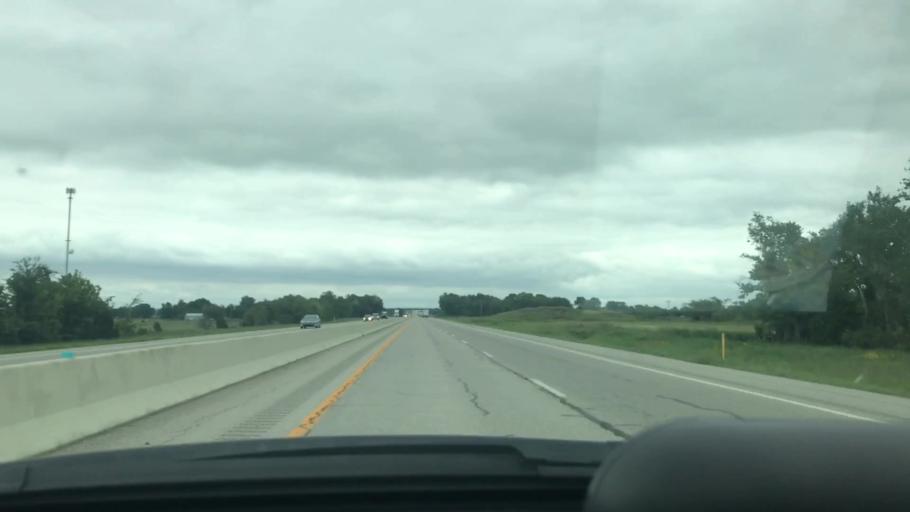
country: US
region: Oklahoma
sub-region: Ottawa County
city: Fairland
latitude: 36.7745
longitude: -94.8931
